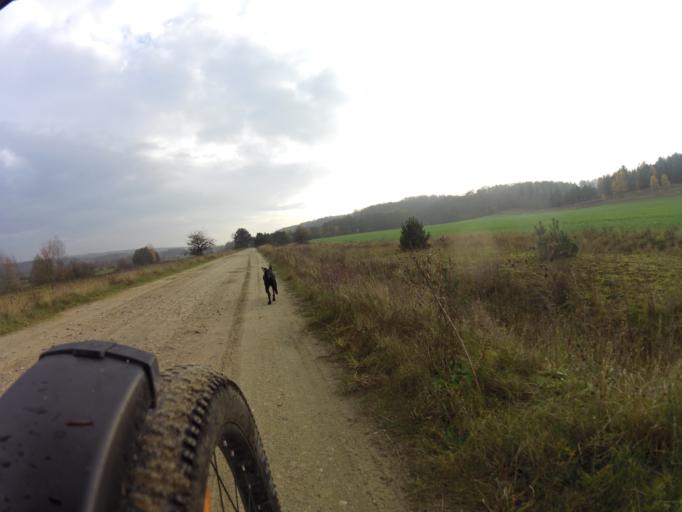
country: PL
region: Pomeranian Voivodeship
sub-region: Powiat wejherowski
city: Gniewino
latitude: 54.7070
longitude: 18.1018
